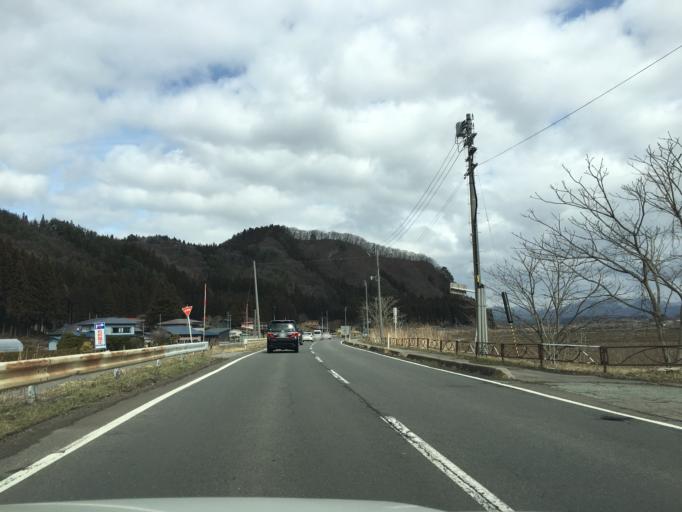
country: JP
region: Akita
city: Hanawa
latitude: 40.2449
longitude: 140.7414
